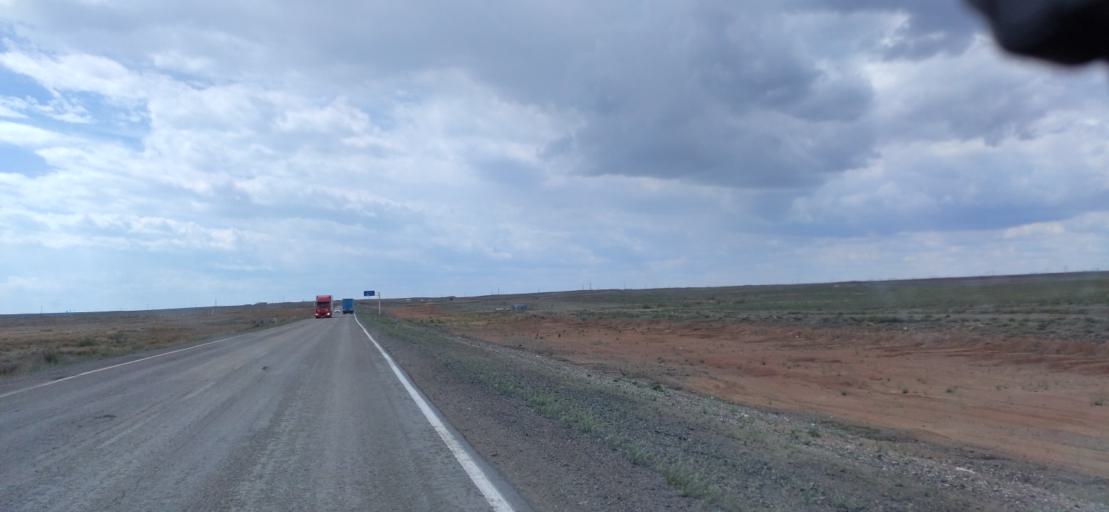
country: KZ
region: Qaraghandy
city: Saryshaghan
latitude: 46.0503
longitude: 73.5962
